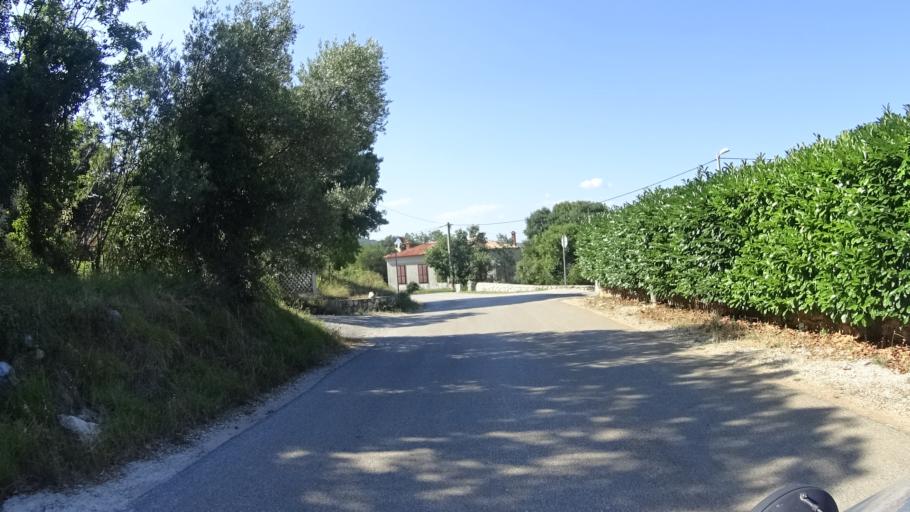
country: HR
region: Istarska
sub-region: Grad Labin
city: Rabac
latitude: 45.0105
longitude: 14.1579
